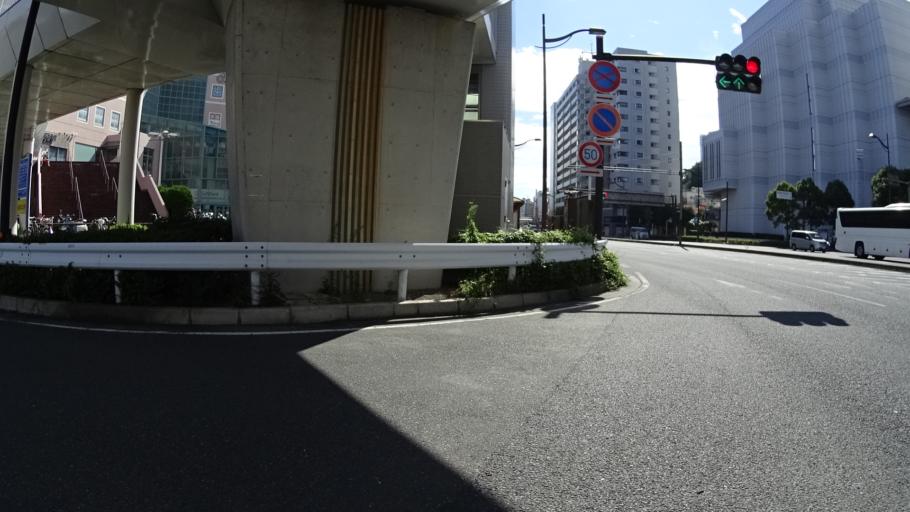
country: JP
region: Kanagawa
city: Yokosuka
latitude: 35.2818
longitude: 139.6619
